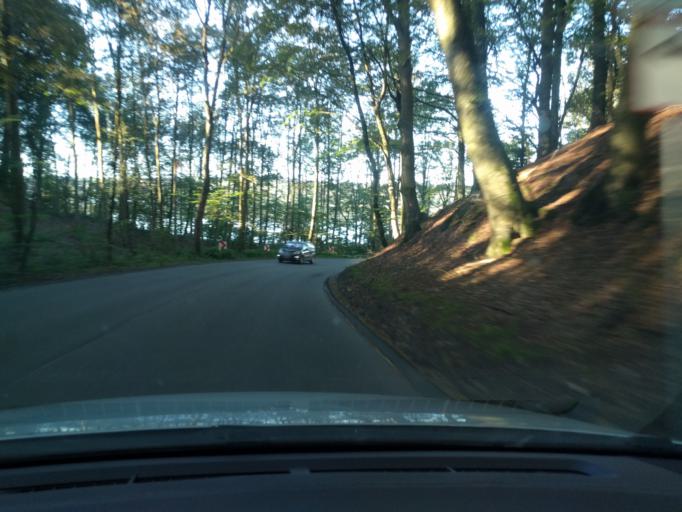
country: DK
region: Central Jutland
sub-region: Skanderborg Kommune
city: Ry
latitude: 56.0962
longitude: 9.7805
